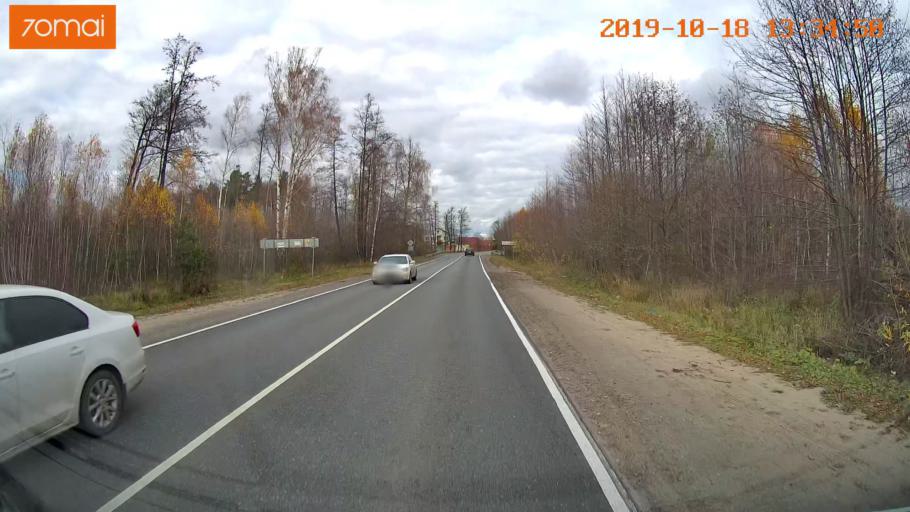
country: RU
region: Rjazan
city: Solotcha
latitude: 54.8567
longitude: 39.9613
